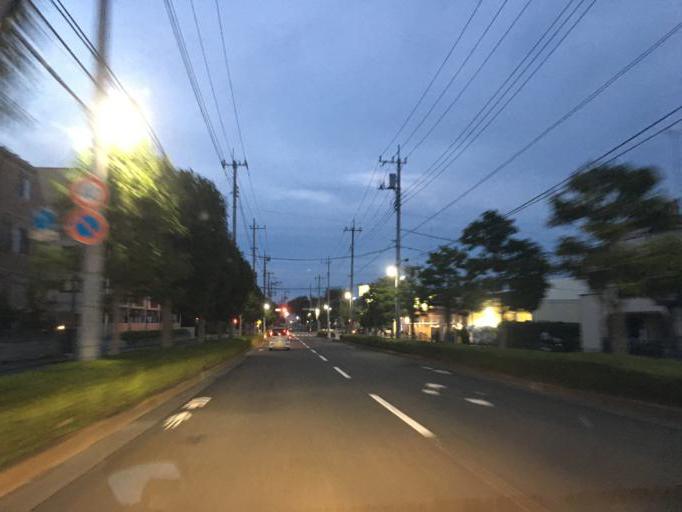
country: JP
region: Tokyo
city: Higashimurayama-shi
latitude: 35.7335
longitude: 139.4528
